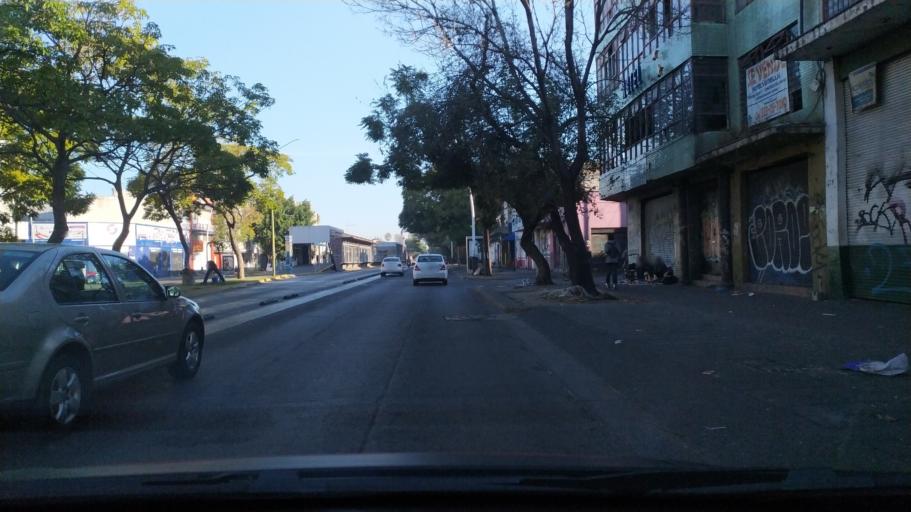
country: MX
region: Jalisco
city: Guadalajara
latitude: 20.6655
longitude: -103.3470
